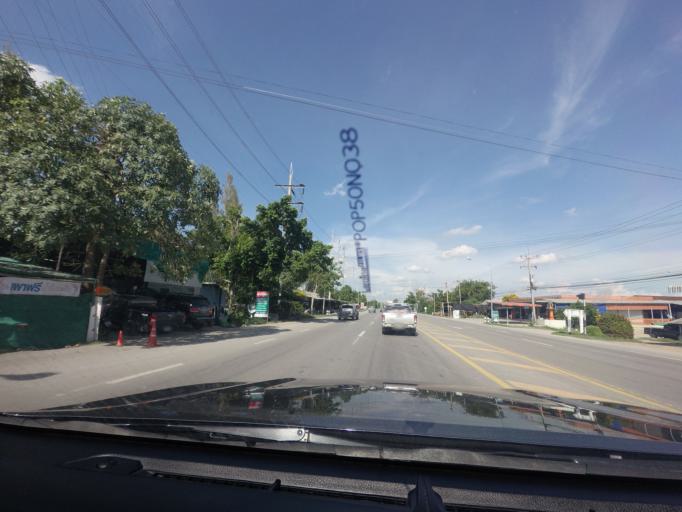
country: TH
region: Nakhon Pathom
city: Bang Len
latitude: 14.1572
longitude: 100.1630
